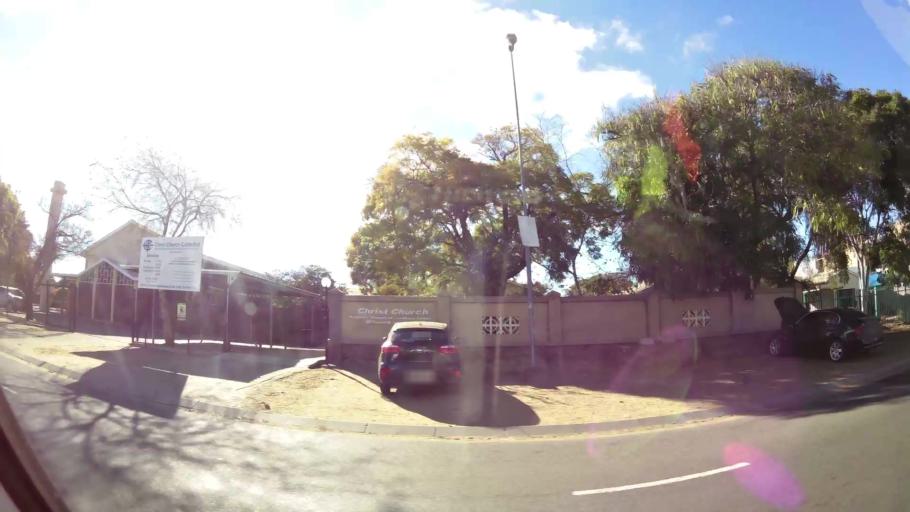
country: ZA
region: Limpopo
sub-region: Capricorn District Municipality
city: Polokwane
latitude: -23.9045
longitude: 29.4553
